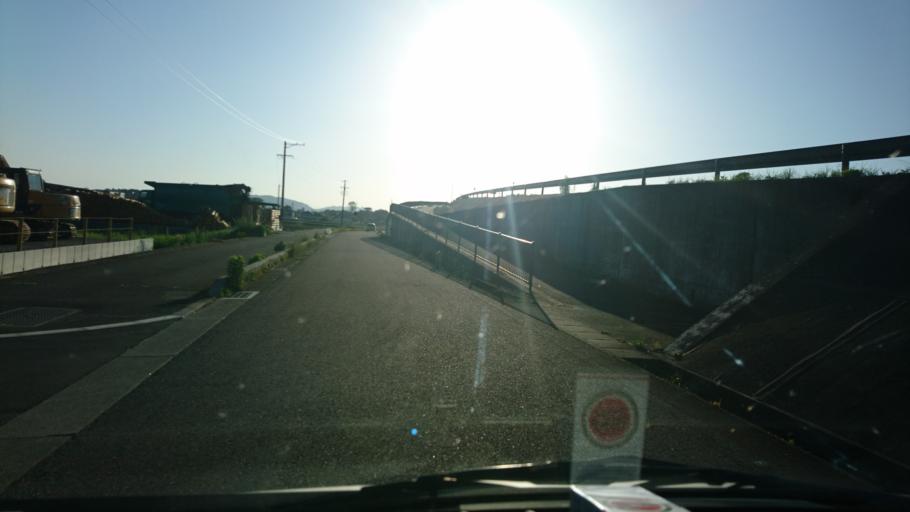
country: JP
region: Gifu
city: Mitake
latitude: 35.4301
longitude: 137.0847
